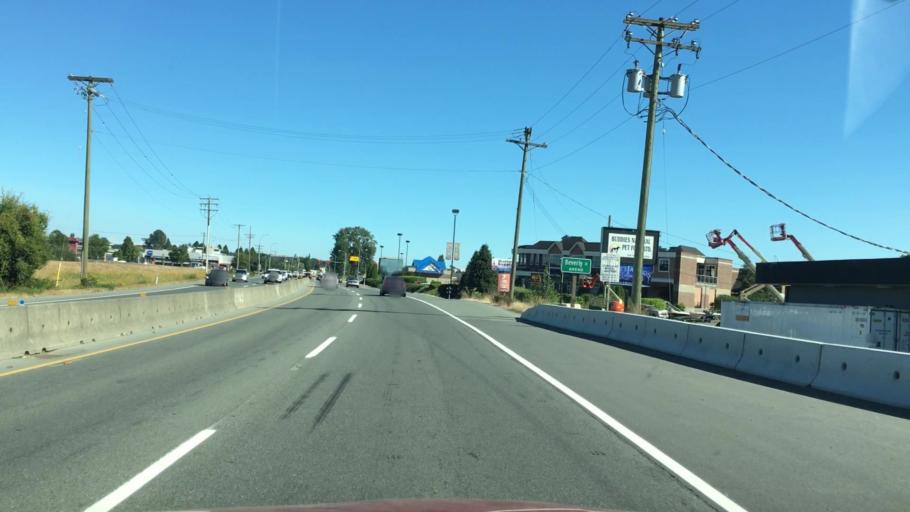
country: CA
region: British Columbia
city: Duncan
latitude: 48.7885
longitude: -123.7096
